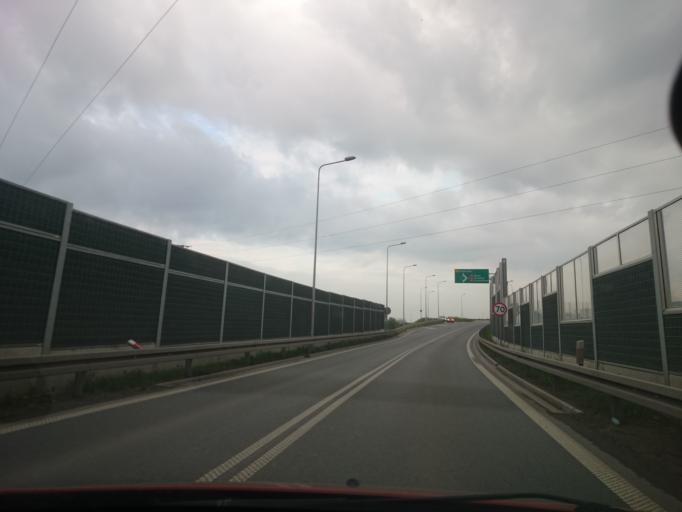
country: PL
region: Opole Voivodeship
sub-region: Powiat opolski
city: Czarnowasy
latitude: 50.6996
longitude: 17.9057
